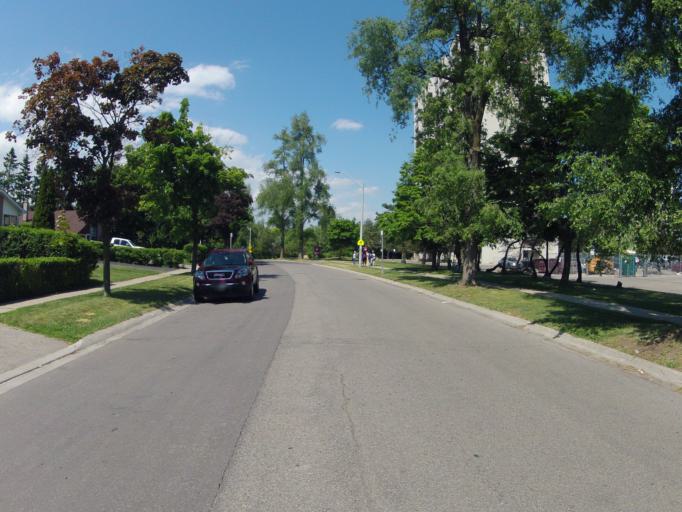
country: CA
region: Ontario
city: Mississauga
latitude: 43.5140
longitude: -79.6491
